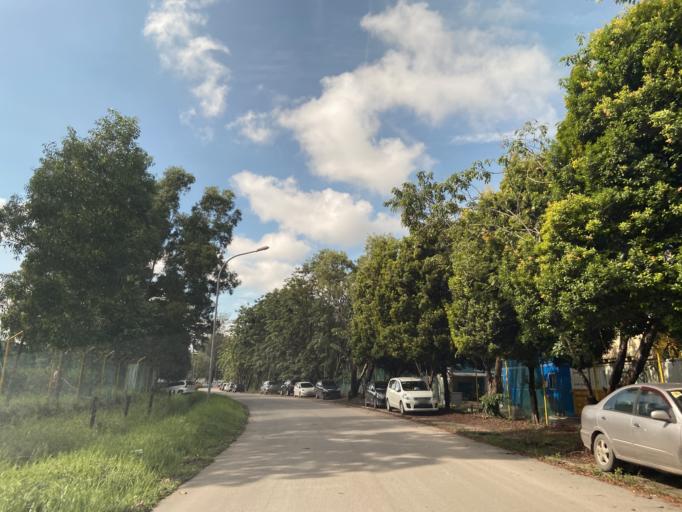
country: SG
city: Singapore
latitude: 1.1757
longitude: 104.0070
